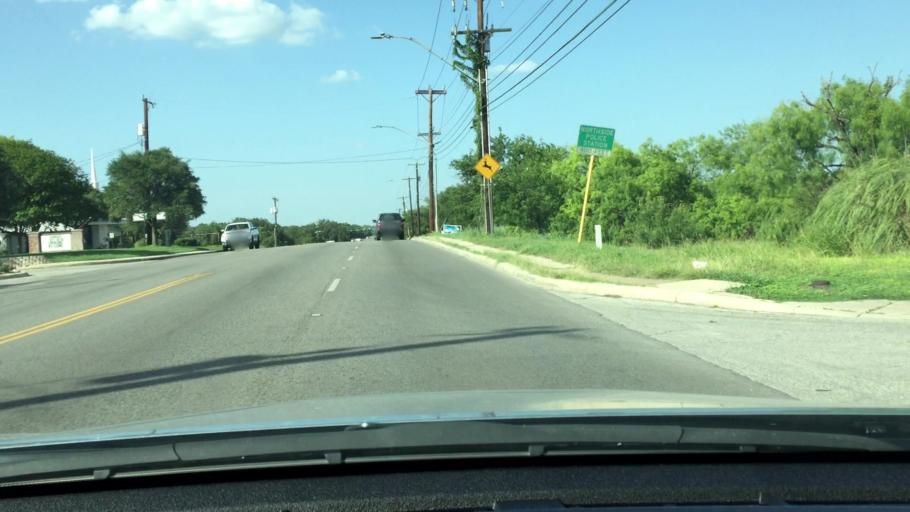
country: US
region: Texas
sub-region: Bexar County
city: Hollywood Park
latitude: 29.5591
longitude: -98.4614
